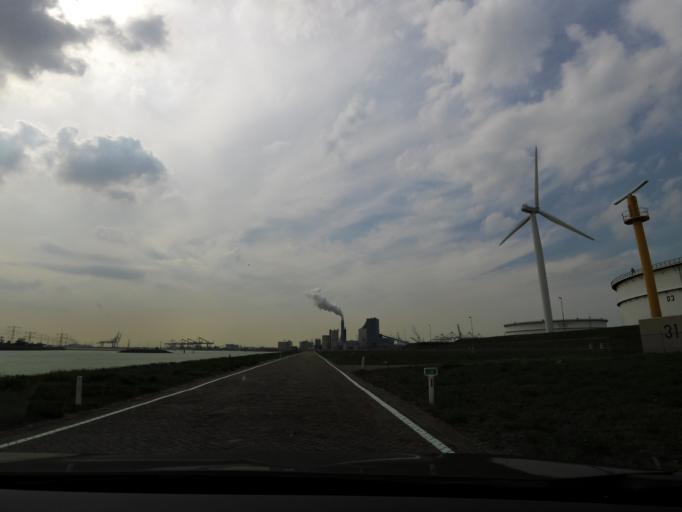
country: NL
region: South Holland
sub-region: Gemeente Rotterdam
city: Hoek van Holland
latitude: 51.9405
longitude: 4.0890
